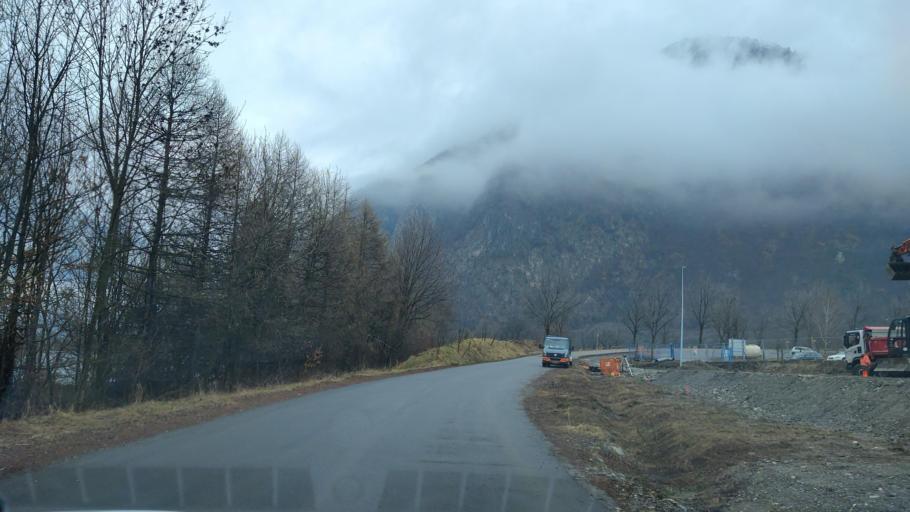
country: FR
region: Rhone-Alpes
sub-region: Departement de la Savoie
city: La Chambre
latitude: 45.3639
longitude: 6.2907
